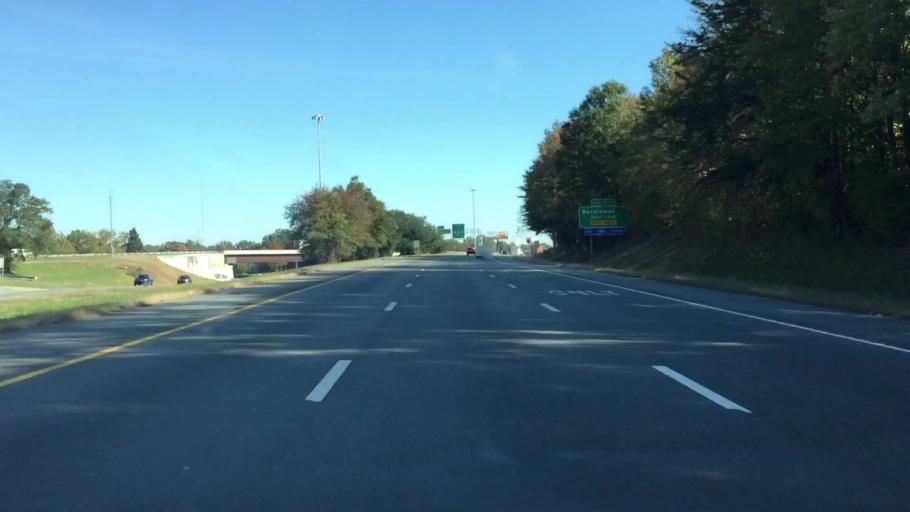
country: US
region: North Carolina
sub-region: Guilford County
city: Greensboro
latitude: 36.0296
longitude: -79.8080
